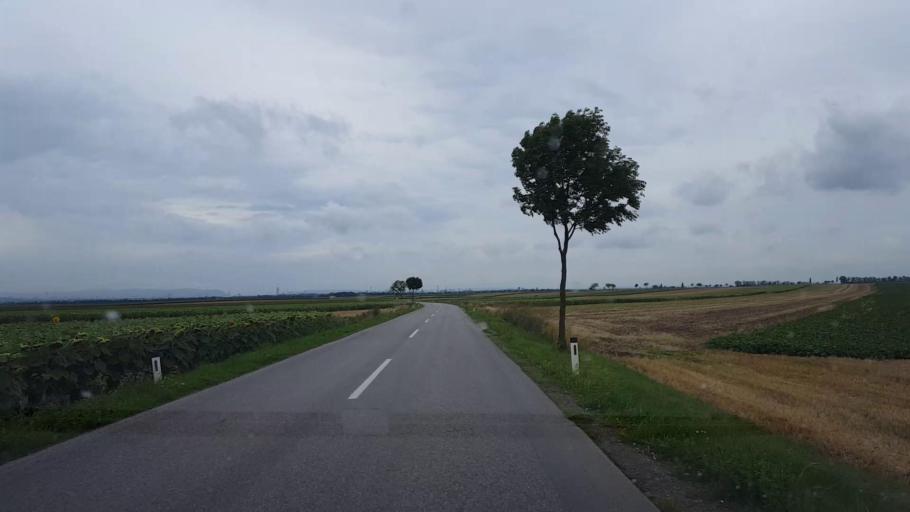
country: AT
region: Lower Austria
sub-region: Politischer Bezirk Wien-Umgebung
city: Rauchenwarth
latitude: 48.0869
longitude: 16.5245
